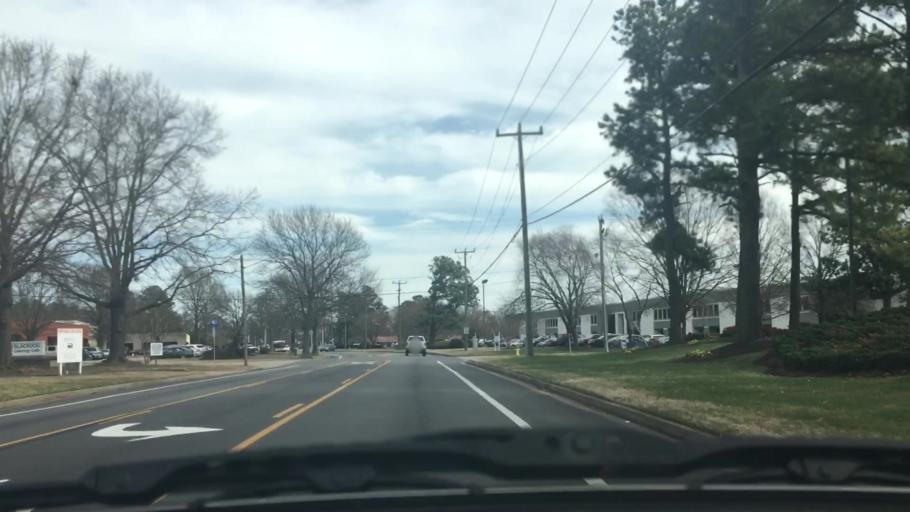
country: US
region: Virginia
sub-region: City of Norfolk
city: Norfolk
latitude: 36.8802
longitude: -76.2206
